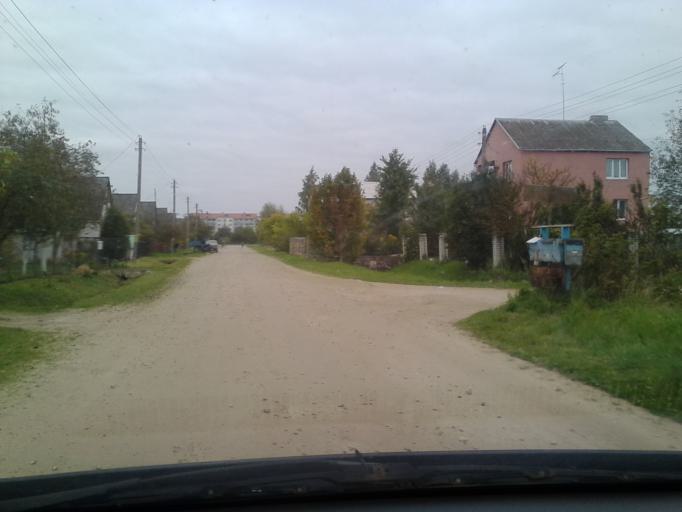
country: BY
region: Vitebsk
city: Pastavy
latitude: 55.1048
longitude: 26.8655
